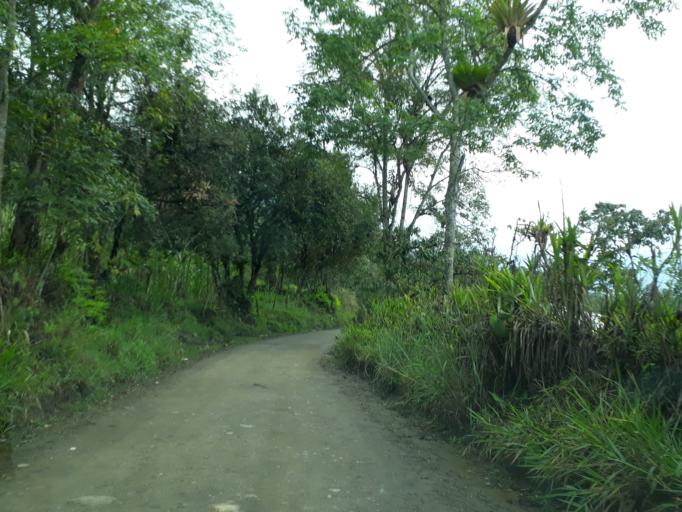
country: CO
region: Cundinamarca
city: Manta
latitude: 4.9924
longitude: -73.5570
